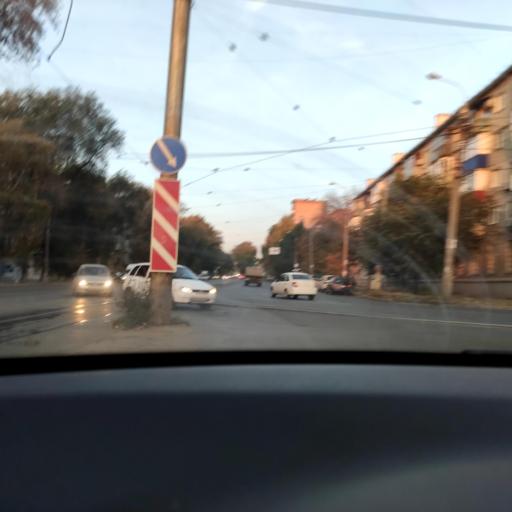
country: RU
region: Samara
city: Samara
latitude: 53.2019
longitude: 50.2318
